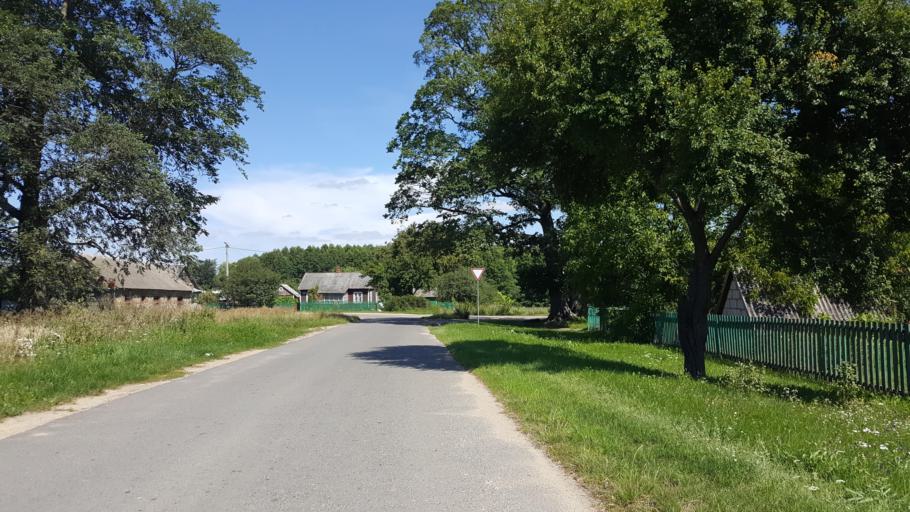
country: BY
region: Brest
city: Charnawchytsy
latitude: 52.3408
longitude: 23.6260
